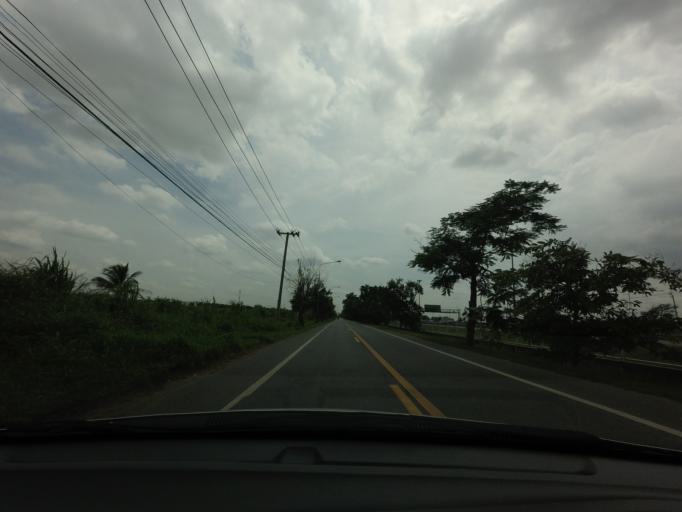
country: TH
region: Bangkok
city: Khan Na Yao
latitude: 13.8753
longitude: 100.6822
